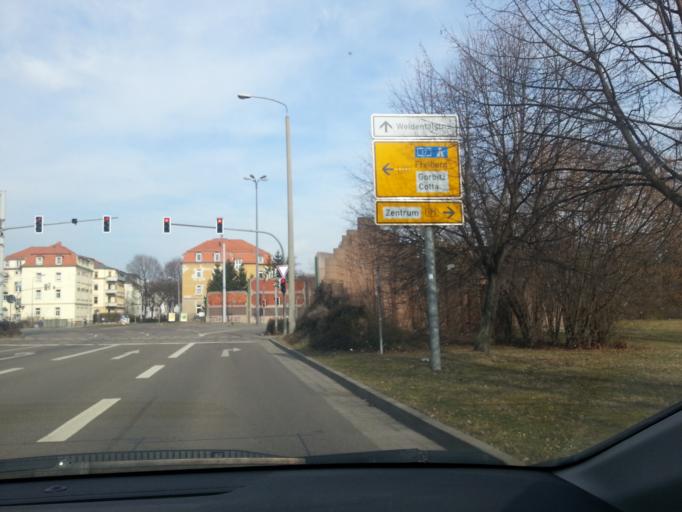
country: DE
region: Saxony
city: Freital
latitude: 51.0480
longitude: 13.6808
